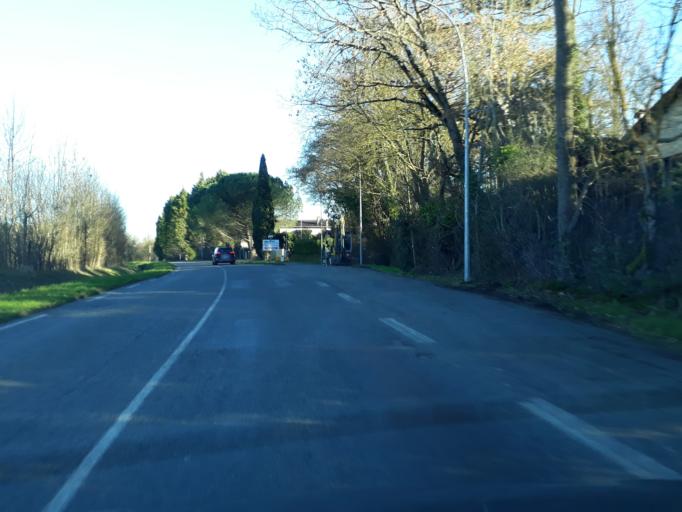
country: FR
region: Midi-Pyrenees
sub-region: Departement du Gers
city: Auch
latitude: 43.6365
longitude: 0.6049
